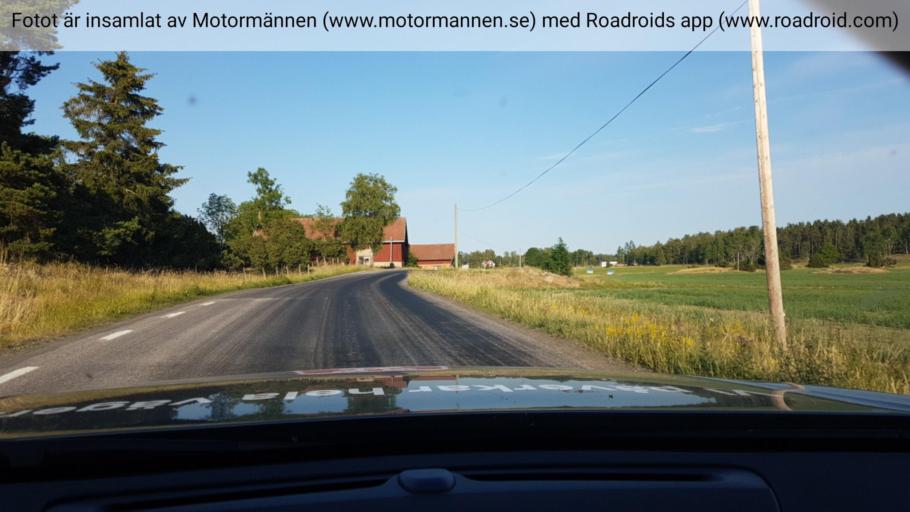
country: SE
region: Uppsala
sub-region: Osthammars Kommun
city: Gimo
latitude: 60.0279
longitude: 18.0539
